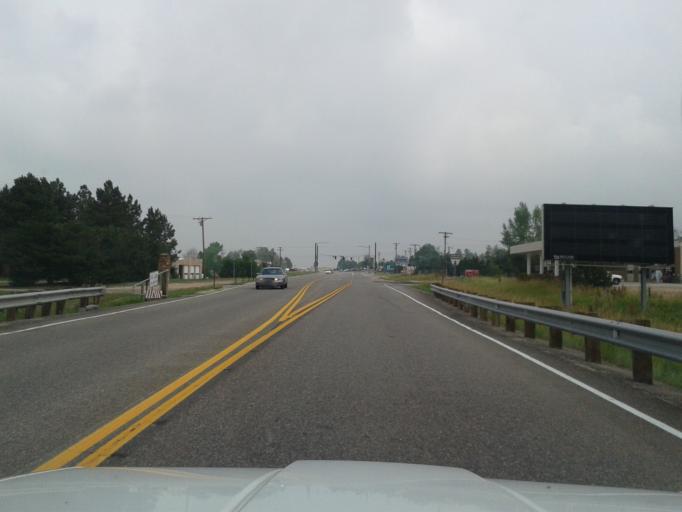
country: US
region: Colorado
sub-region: Douglas County
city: The Pinery
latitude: 39.3887
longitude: -104.7524
